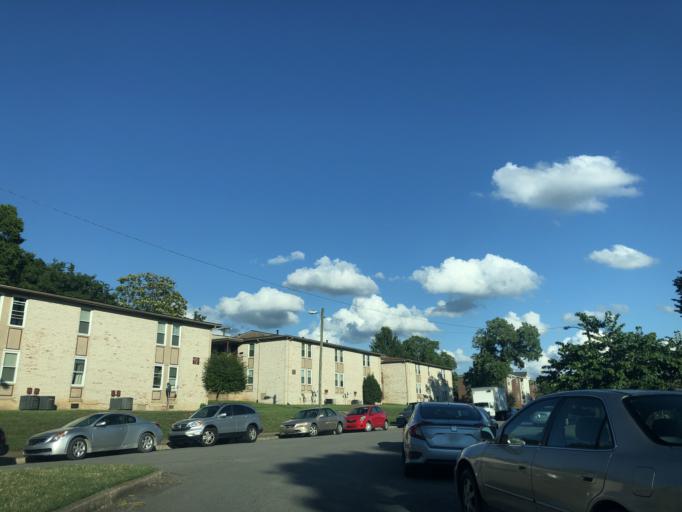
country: US
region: Tennessee
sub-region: Davidson County
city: Nashville
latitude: 36.1793
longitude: -86.7613
